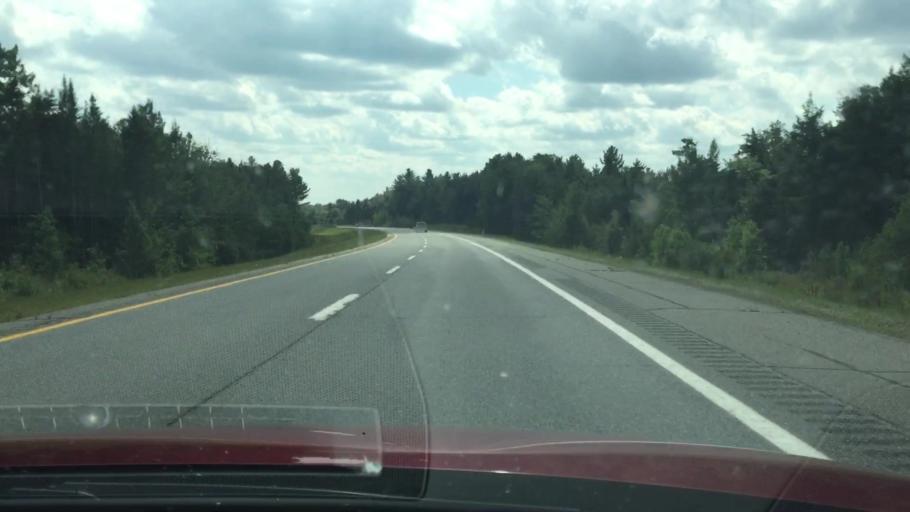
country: US
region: Maine
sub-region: Penobscot County
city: Howland
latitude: 45.2727
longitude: -68.6782
